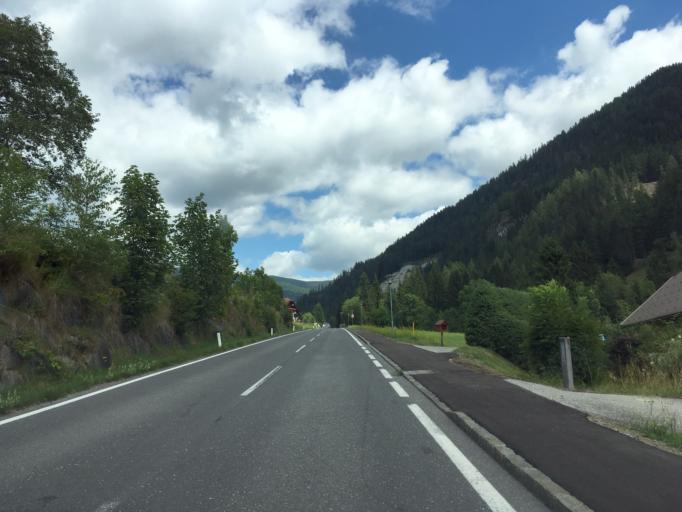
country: AT
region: Carinthia
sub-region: Politischer Bezirk Spittal an der Drau
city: Kleinkirchheim
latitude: 46.8225
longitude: 13.7707
